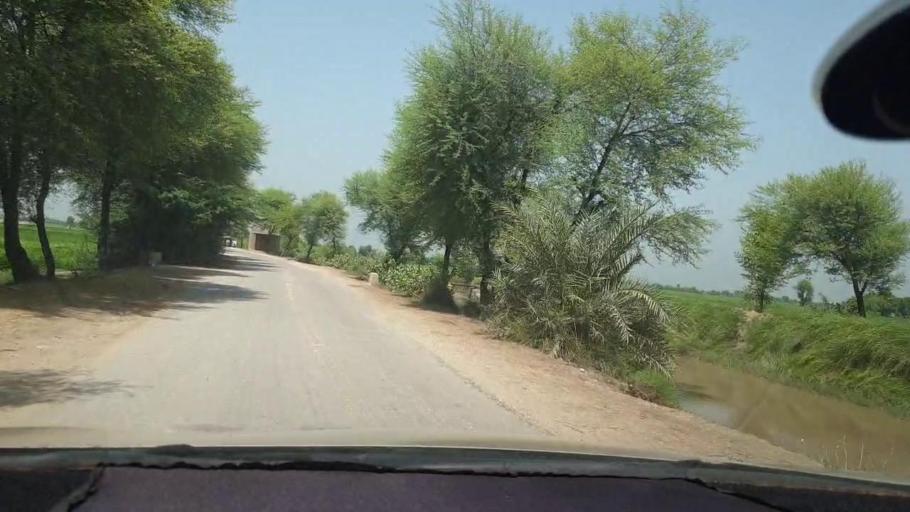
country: PK
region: Sindh
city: Kambar
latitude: 27.6377
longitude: 67.9777
